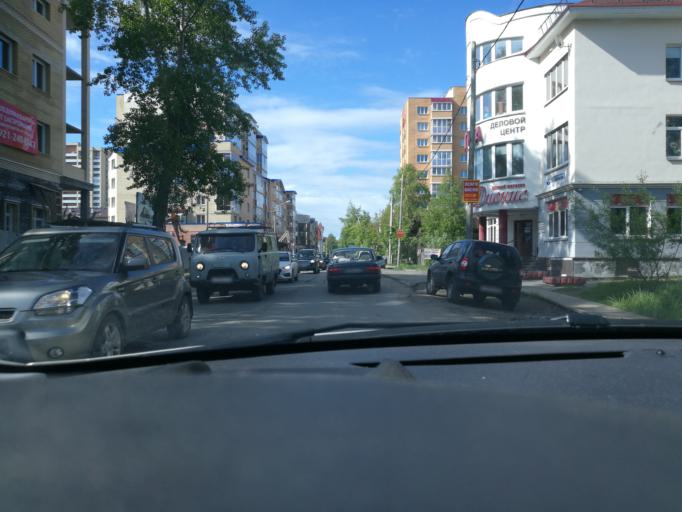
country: RU
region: Arkhangelskaya
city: Arkhangel'sk
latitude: 64.5402
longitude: 40.5342
